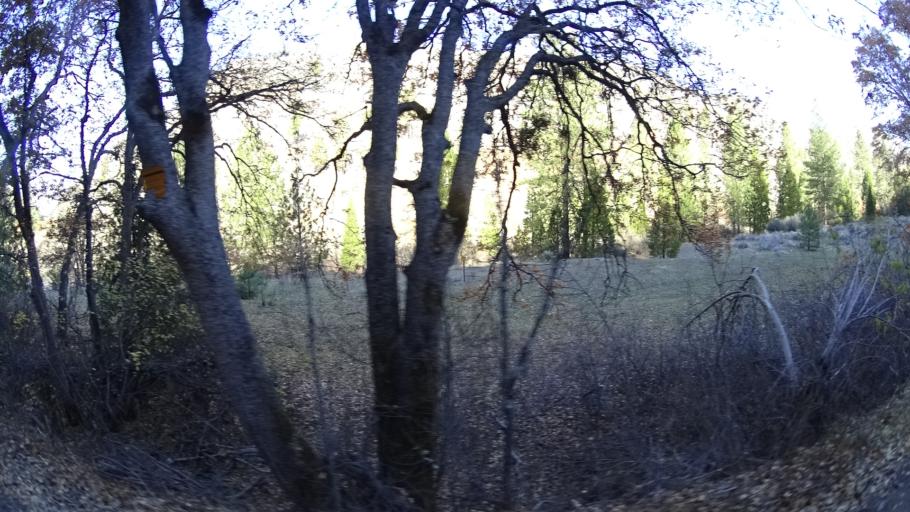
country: US
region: California
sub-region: Siskiyou County
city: Yreka
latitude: 41.8538
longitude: -122.7663
